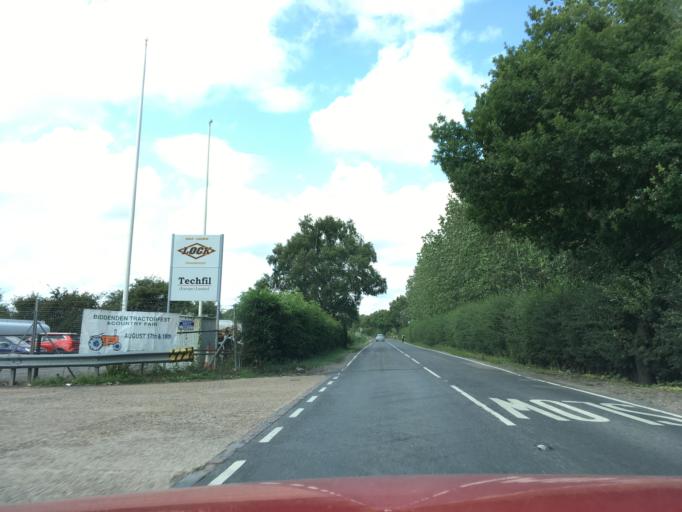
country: GB
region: England
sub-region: Kent
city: Headcorn
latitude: 51.1621
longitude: 0.6331
